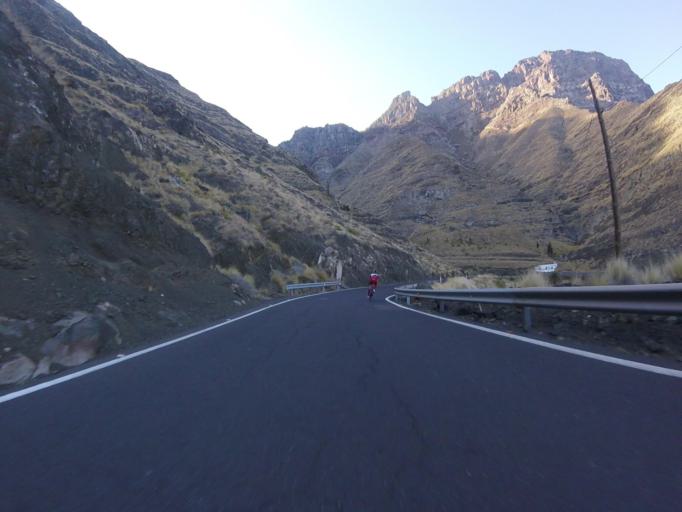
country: ES
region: Canary Islands
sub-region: Provincia de Las Palmas
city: Agaete
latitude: 28.0720
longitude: -15.7109
